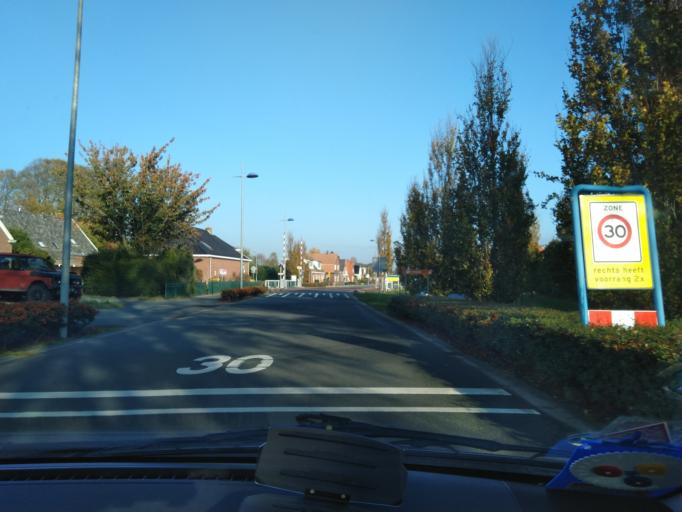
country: NL
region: Groningen
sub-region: Gemeente Hoogezand-Sappemeer
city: Hoogezand
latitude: 53.1230
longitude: 6.7704
